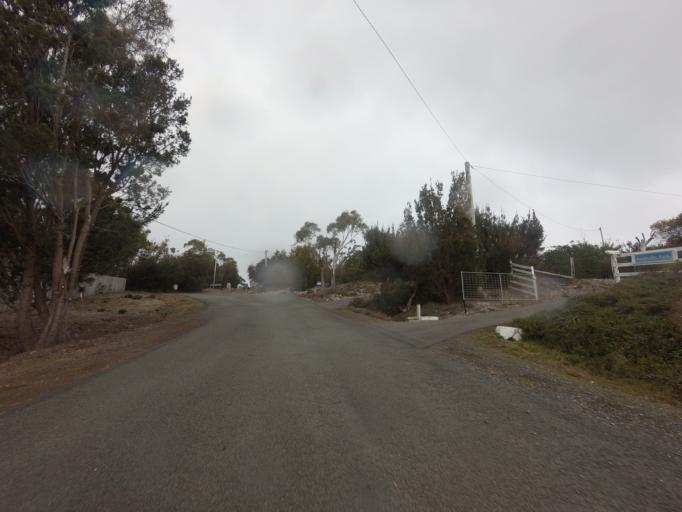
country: AU
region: Tasmania
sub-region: Sorell
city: Sorell
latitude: -42.5362
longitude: 147.9123
